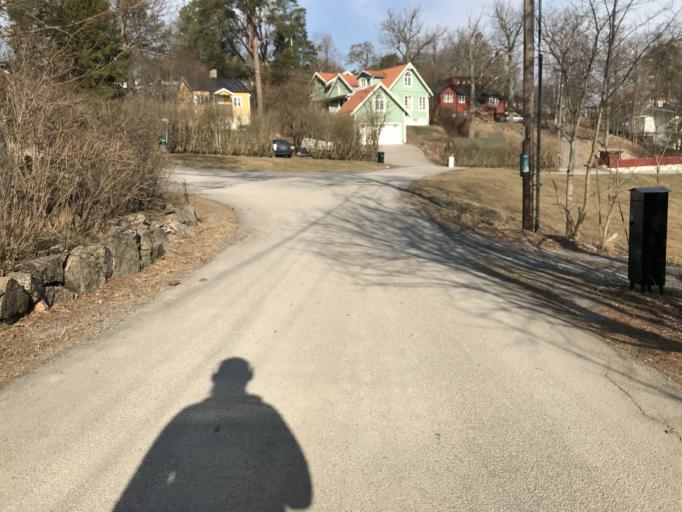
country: SE
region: Stockholm
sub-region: Osterakers Kommun
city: Akersberga
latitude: 59.4733
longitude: 18.3057
